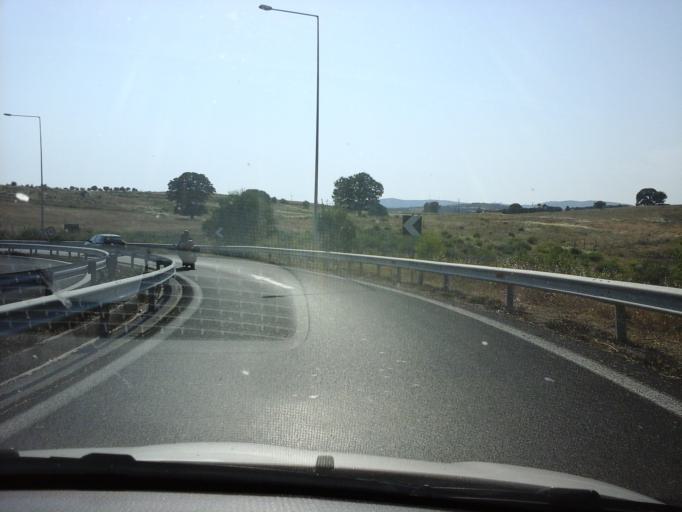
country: GR
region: East Macedonia and Thrace
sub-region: Nomos Evrou
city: Alexandroupoli
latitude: 40.8793
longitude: 25.8587
